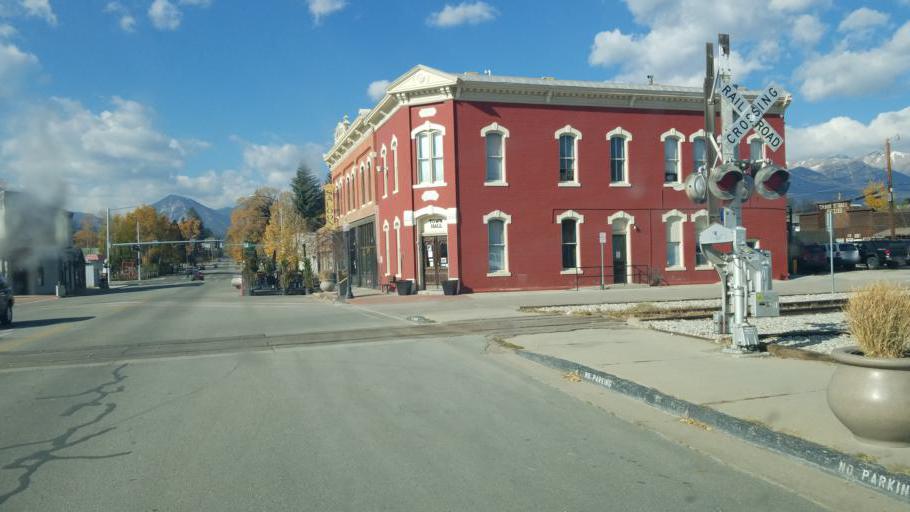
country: US
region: Colorado
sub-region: Chaffee County
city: Buena Vista
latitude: 38.8423
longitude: -106.1312
